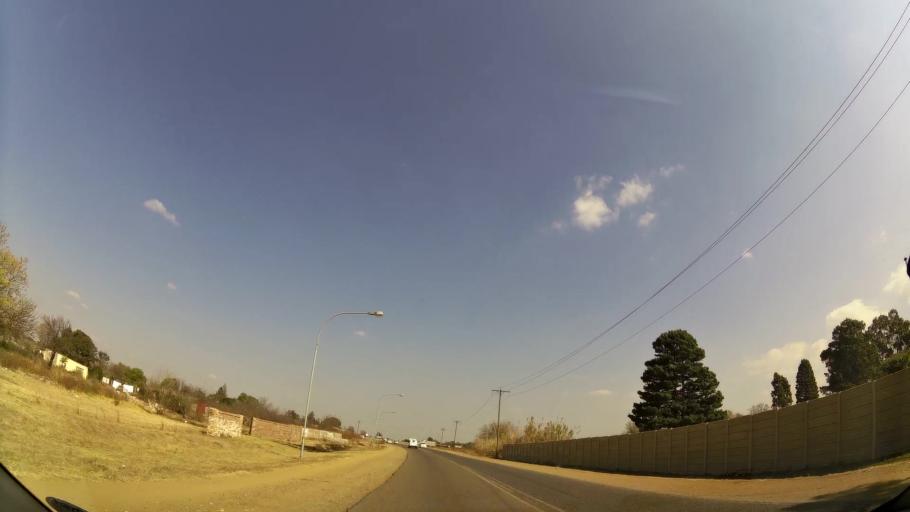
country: ZA
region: Gauteng
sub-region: Ekurhuleni Metropolitan Municipality
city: Benoni
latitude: -26.1234
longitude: 28.3948
